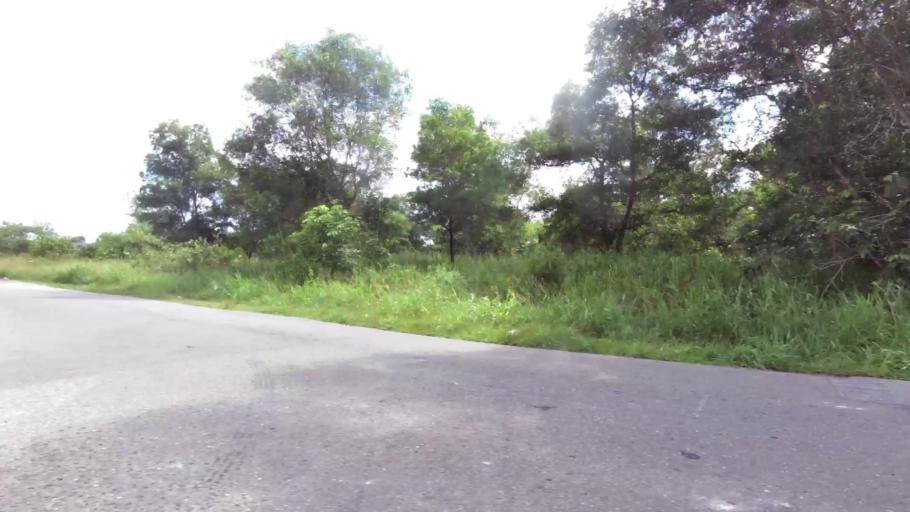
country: BN
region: Brunei and Muara
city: Bandar Seri Begawan
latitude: 4.9376
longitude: 114.9042
